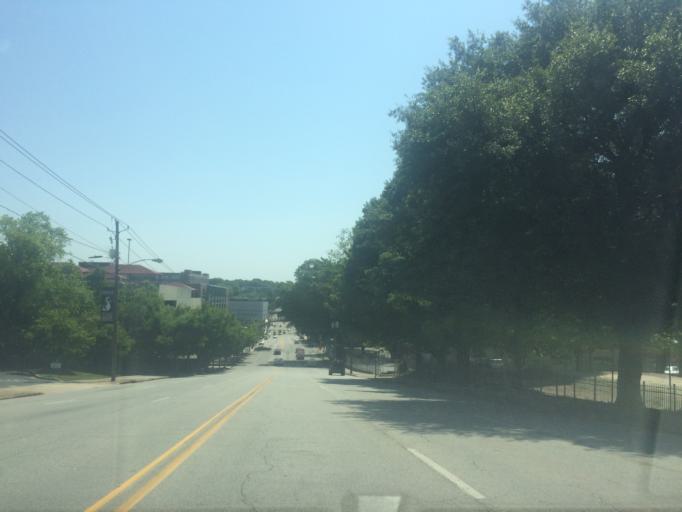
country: US
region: Georgia
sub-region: Fulton County
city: Atlanta
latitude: 33.7711
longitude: -84.3696
